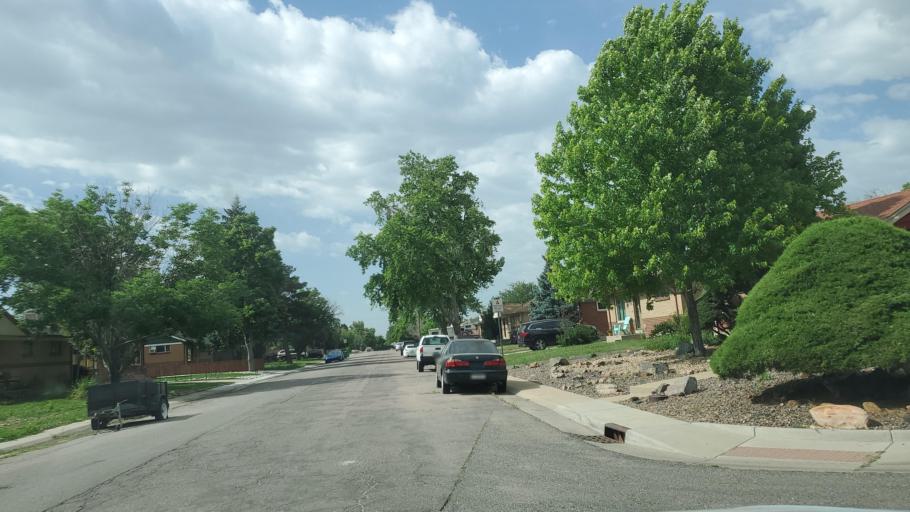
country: US
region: Colorado
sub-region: Adams County
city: Twin Lakes
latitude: 39.8294
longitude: -105.0108
